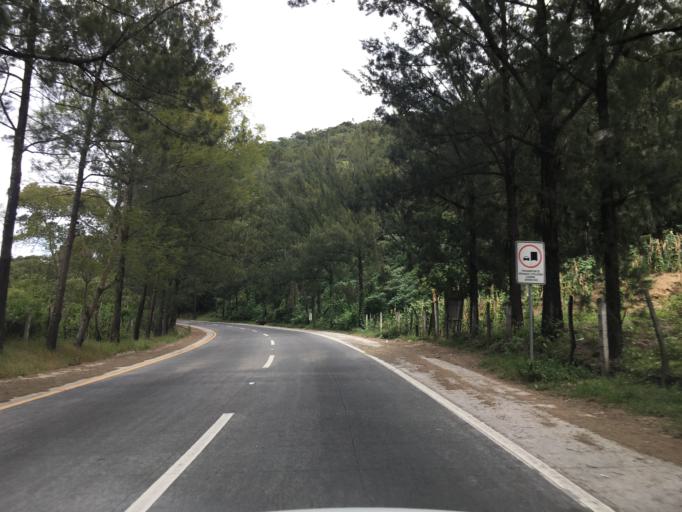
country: GT
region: Sacatepequez
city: Antigua Guatemala
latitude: 14.5584
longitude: -90.7126
